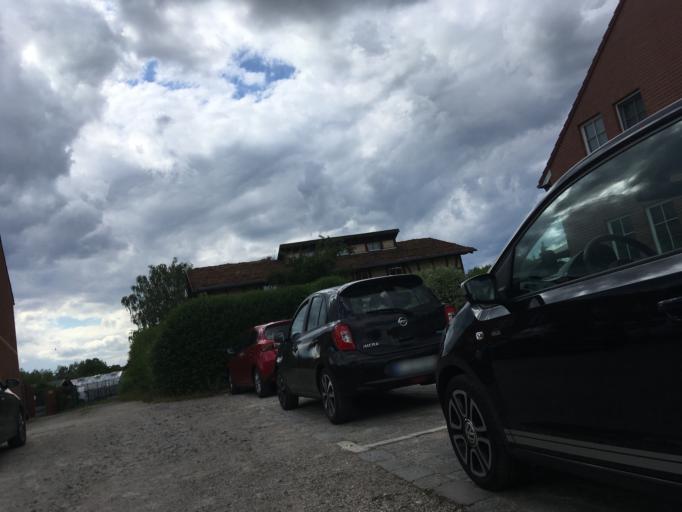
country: DE
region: Berlin
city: Falkenberg
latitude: 52.5709
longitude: 13.5332
